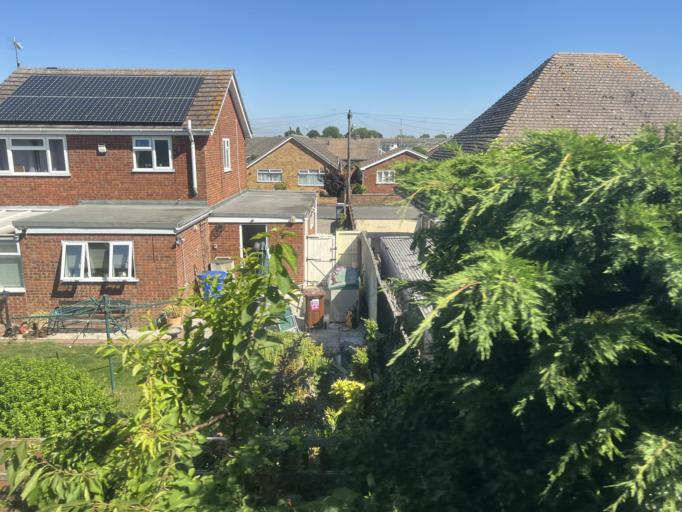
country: GB
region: England
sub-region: Lincolnshire
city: Boston
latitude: 52.9692
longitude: -0.0384
